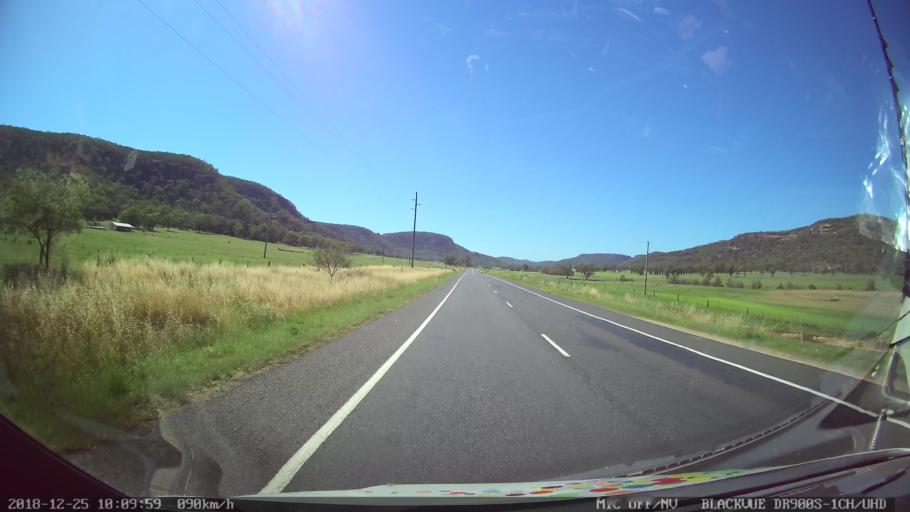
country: AU
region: New South Wales
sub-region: Muswellbrook
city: Denman
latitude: -32.2982
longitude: 150.5187
